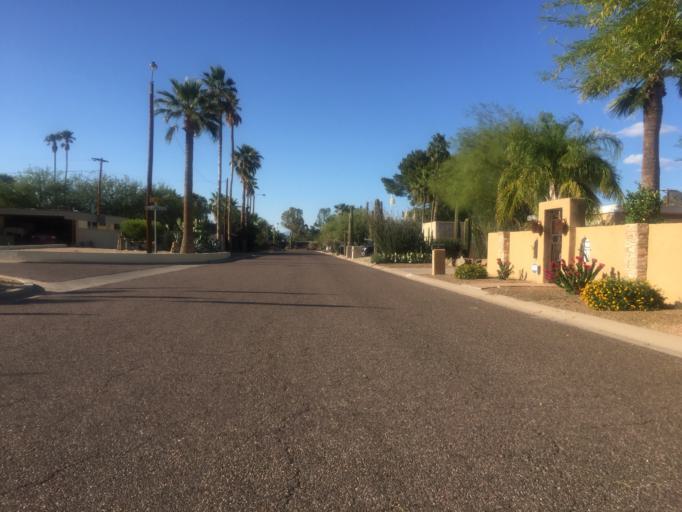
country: US
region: Arizona
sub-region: Maricopa County
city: Paradise Valley
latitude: 33.5768
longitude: -112.0056
